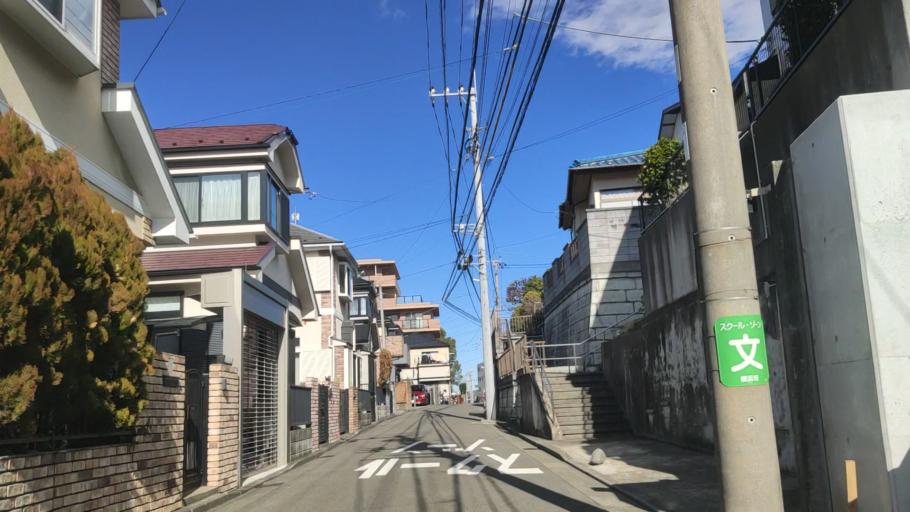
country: JP
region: Kanagawa
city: Yokohama
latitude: 35.4773
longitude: 139.5787
